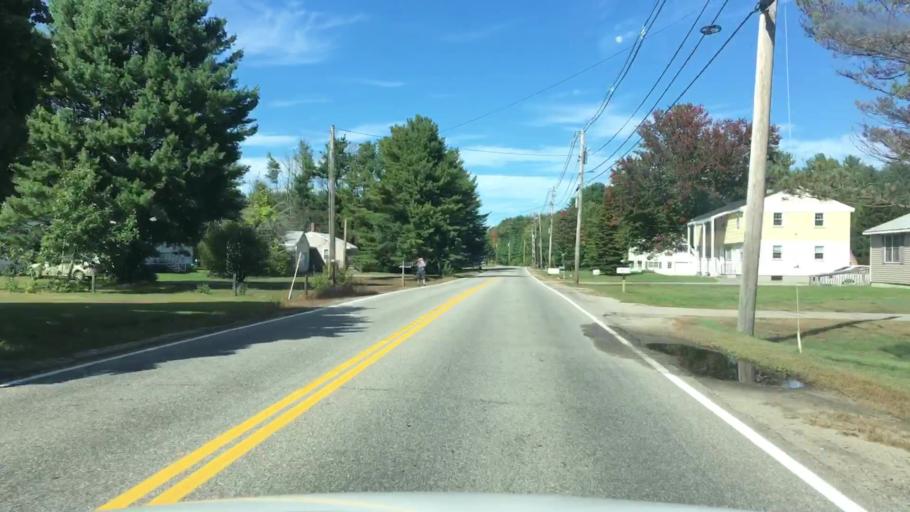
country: US
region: Maine
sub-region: Cumberland County
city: Westbrook
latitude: 43.6434
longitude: -70.3978
